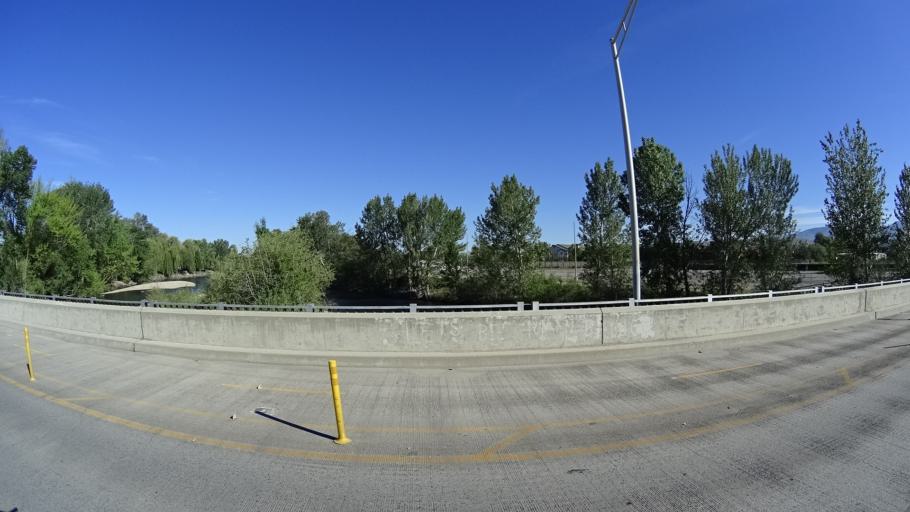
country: US
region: Idaho
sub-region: Ada County
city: Garden City
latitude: 43.6206
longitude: -116.2307
